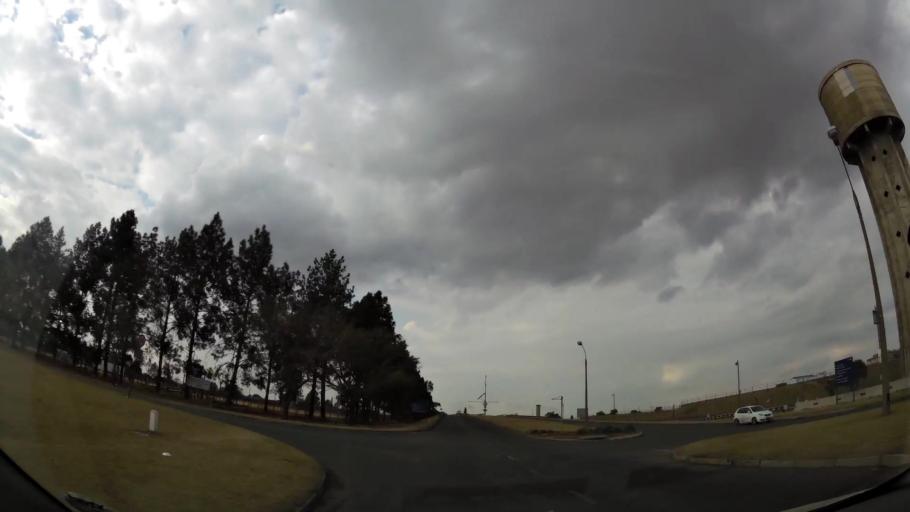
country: ZA
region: Orange Free State
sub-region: Fezile Dabi District Municipality
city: Sasolburg
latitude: -26.8183
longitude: 27.8406
